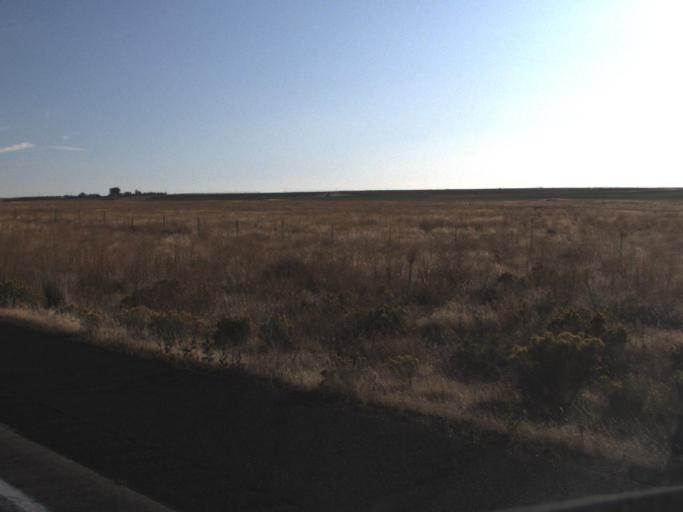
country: US
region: Washington
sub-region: Franklin County
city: Connell
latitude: 46.6119
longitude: -118.9109
